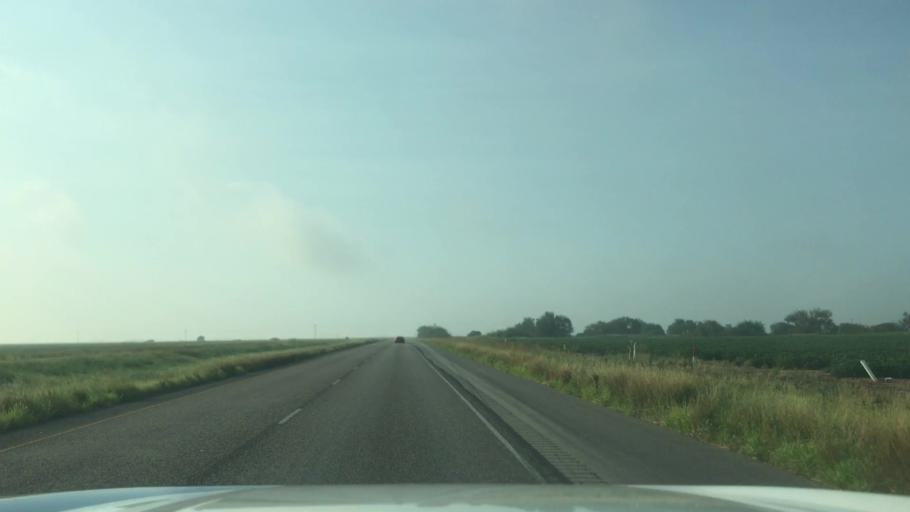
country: US
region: Texas
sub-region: Lubbock County
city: Slaton
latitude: 33.3495
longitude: -101.5485
